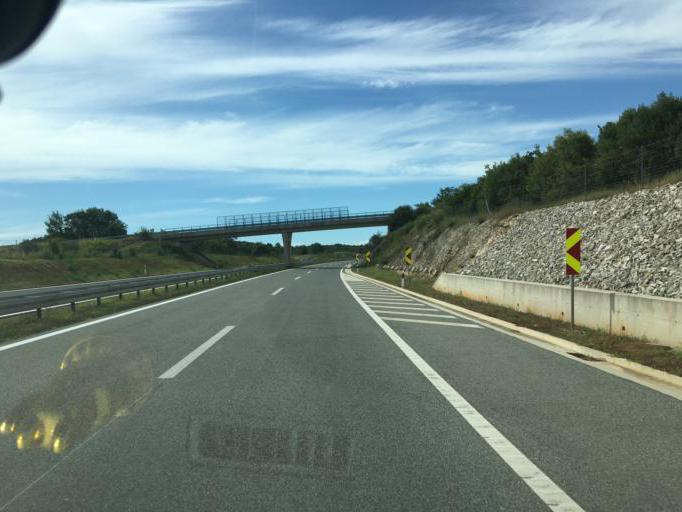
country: HR
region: Istarska
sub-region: Grad Rovinj
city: Rovinj
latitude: 45.1275
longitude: 13.7738
